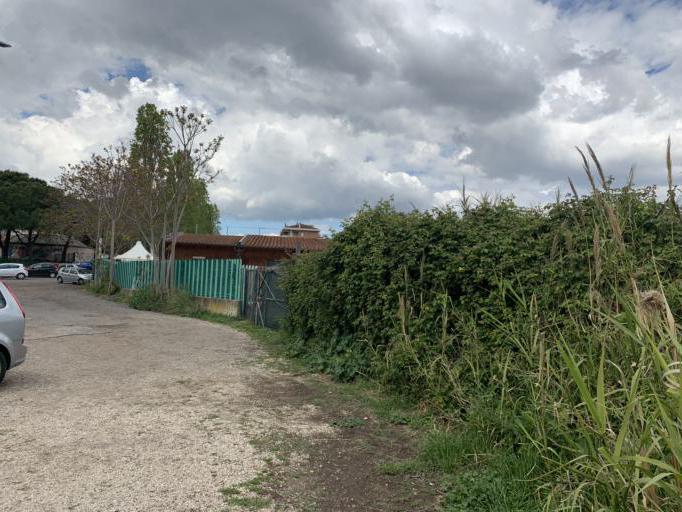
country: VA
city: Vatican City
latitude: 41.8825
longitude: 12.4266
